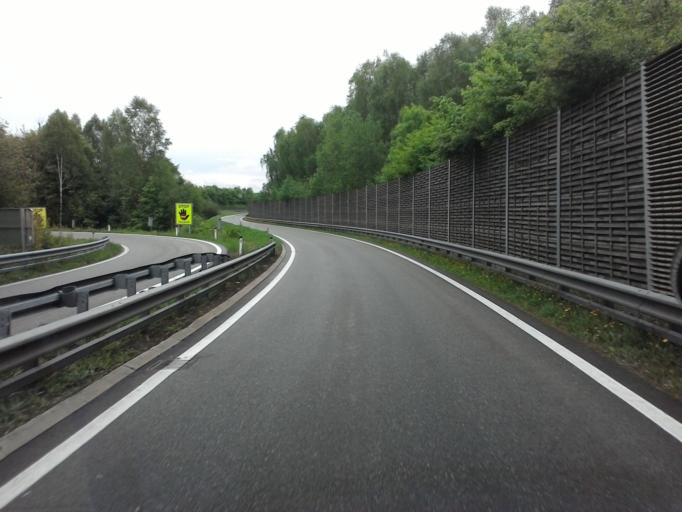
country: AT
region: Upper Austria
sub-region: Politischer Bezirk Scharding
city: Sankt Marienkirchen bei Schaerding
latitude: 48.3179
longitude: 13.4176
